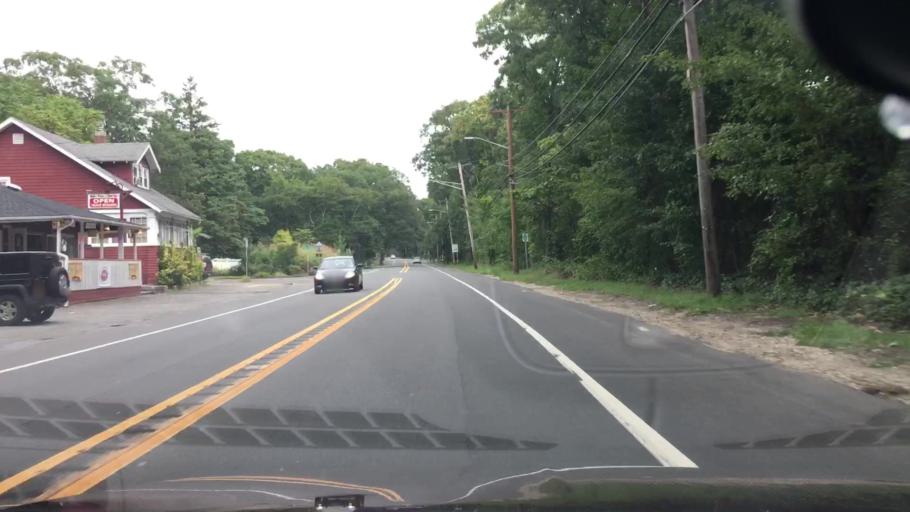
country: US
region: New York
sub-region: Suffolk County
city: Village of the Branch
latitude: 40.8628
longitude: -73.1796
